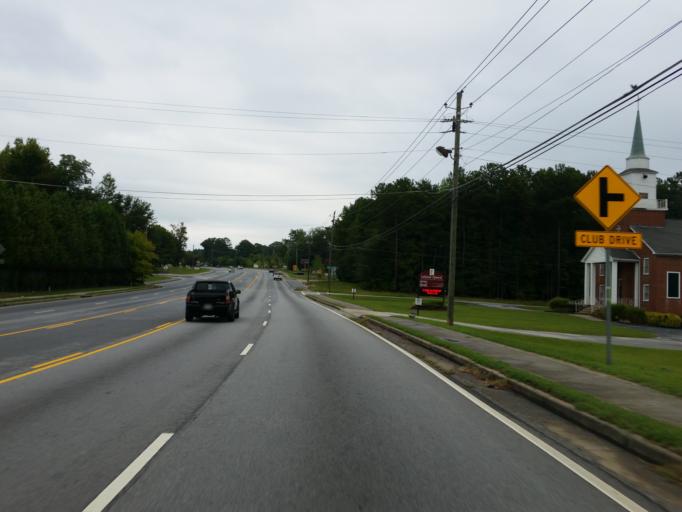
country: US
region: Georgia
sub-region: Cobb County
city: Mableton
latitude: 33.8121
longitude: -84.5578
